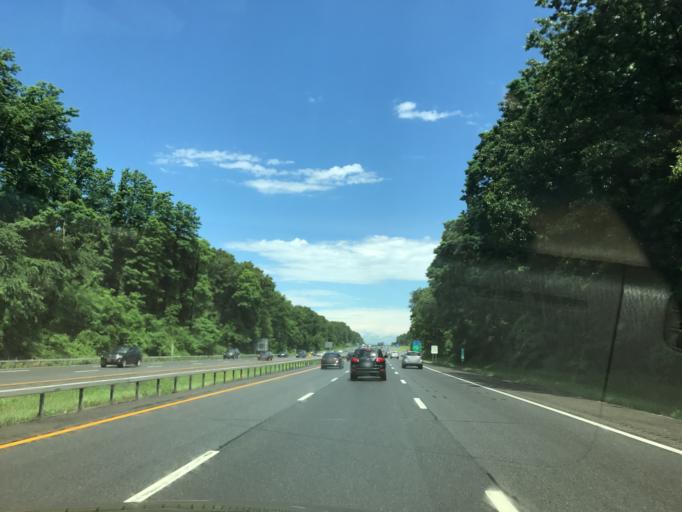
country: US
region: New York
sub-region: Saratoga County
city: Country Knolls
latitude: 42.8699
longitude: -73.7763
